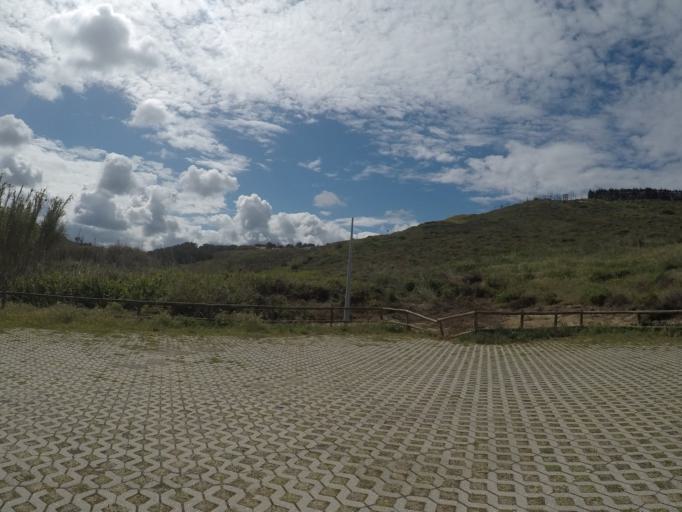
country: PT
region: Beja
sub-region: Odemira
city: Sao Teotonio
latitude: 37.4994
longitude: -8.7899
